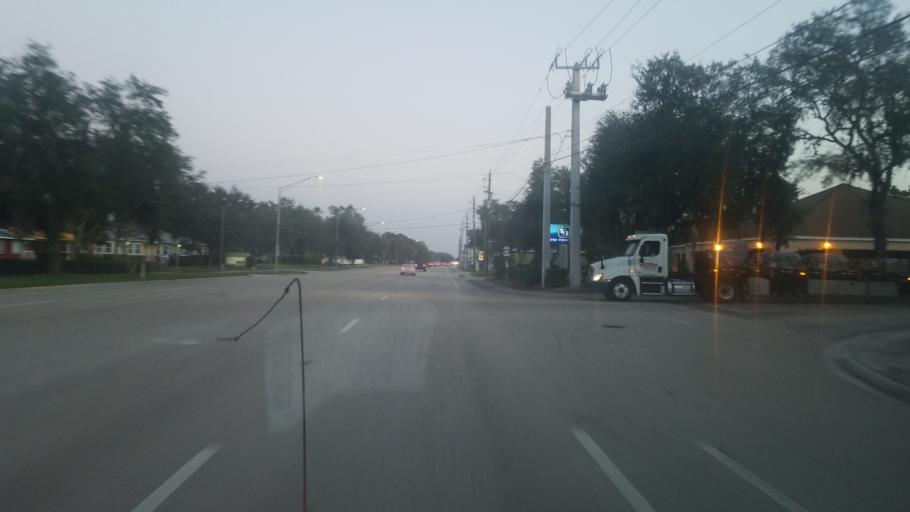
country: US
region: Florida
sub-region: Sarasota County
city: Fruitville
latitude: 27.3138
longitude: -82.4514
